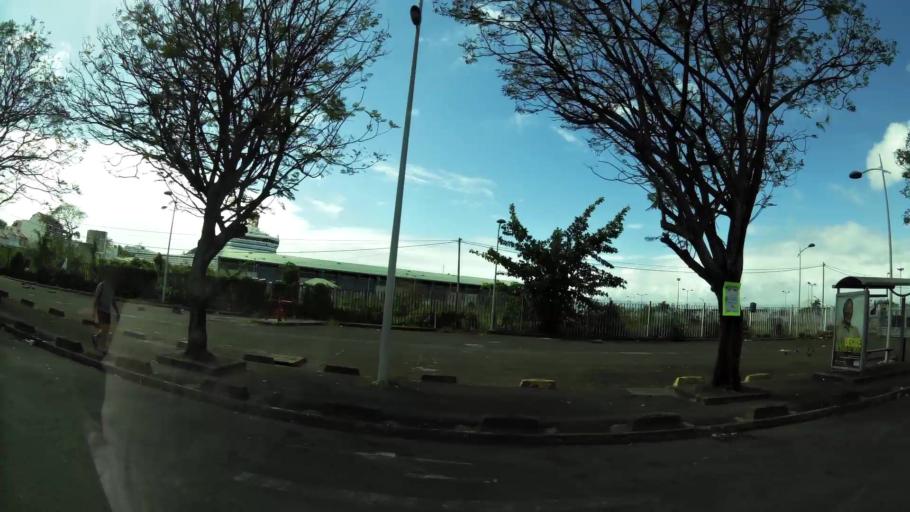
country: GP
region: Guadeloupe
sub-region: Guadeloupe
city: Pointe-a-Pitre
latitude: 16.2419
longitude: -61.5387
